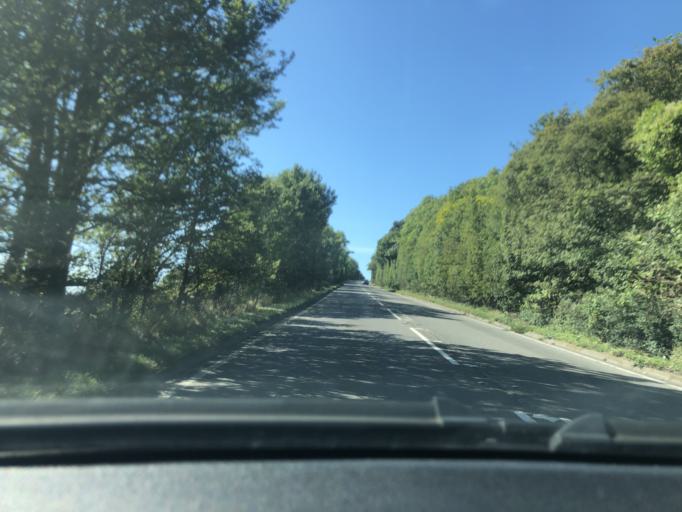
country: GB
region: England
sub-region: Somerset
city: Puriton
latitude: 51.1619
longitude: -2.9668
